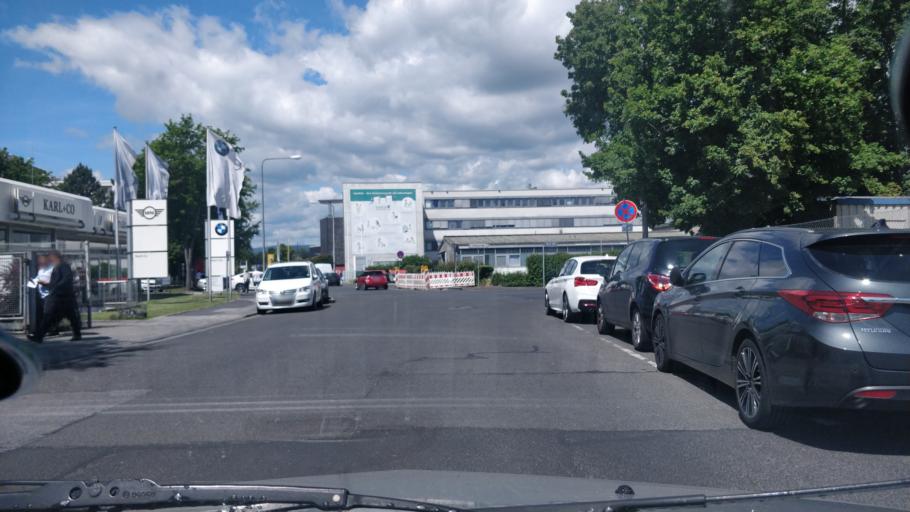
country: DE
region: Hesse
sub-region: Regierungsbezirk Darmstadt
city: Wiesbaden
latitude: 50.0426
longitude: 8.2218
